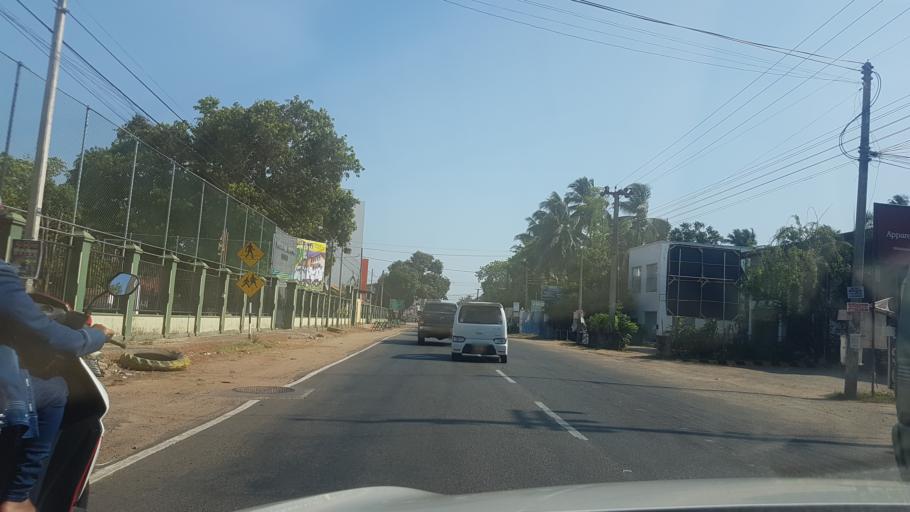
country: LK
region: North Western
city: Chilaw
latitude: 7.4160
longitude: 79.8306
